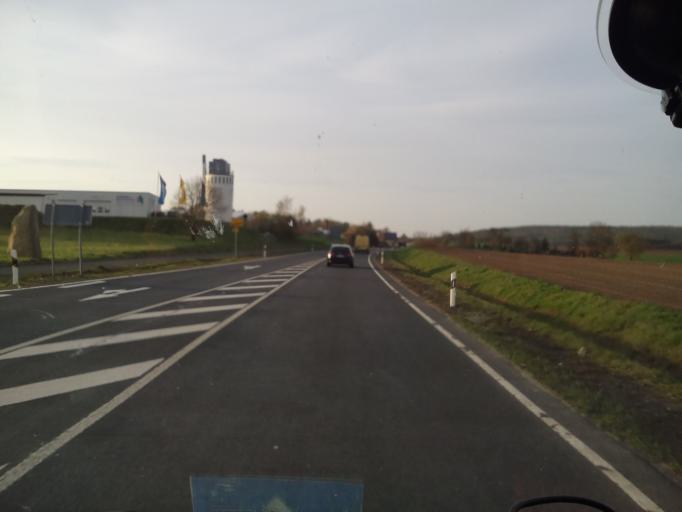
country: DE
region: Bavaria
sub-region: Upper Franconia
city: Reckendorf
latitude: 50.0231
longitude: 10.8265
